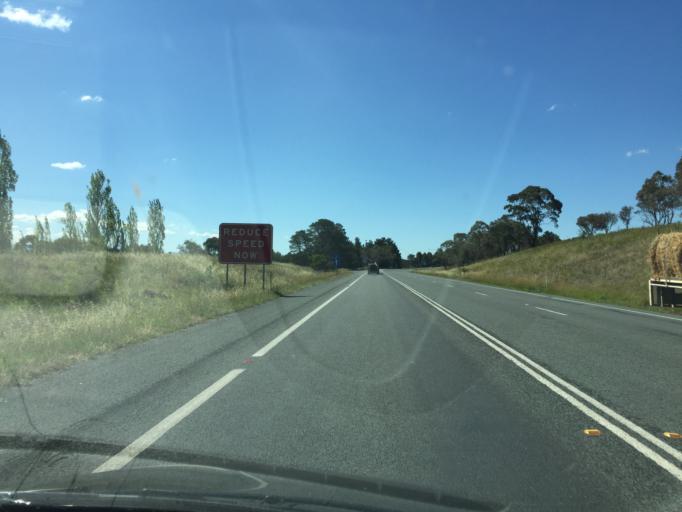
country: AU
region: Australian Capital Territory
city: Macarthur
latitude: -35.4399
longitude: 149.1277
